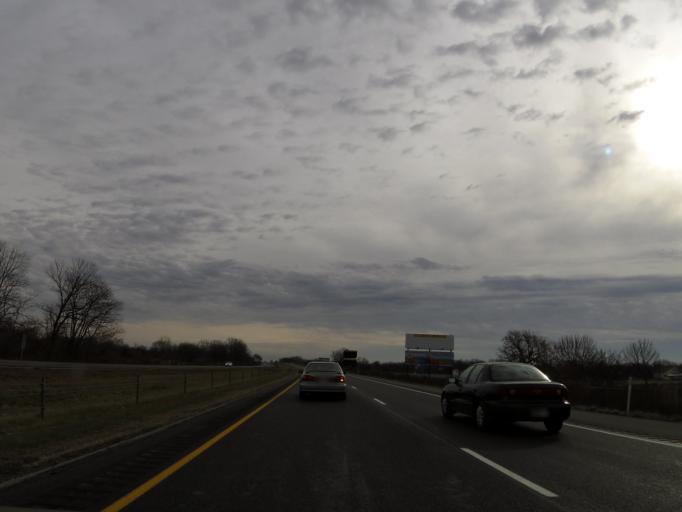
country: US
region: Indiana
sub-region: Marion County
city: Clermont
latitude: 39.8344
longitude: -86.3417
